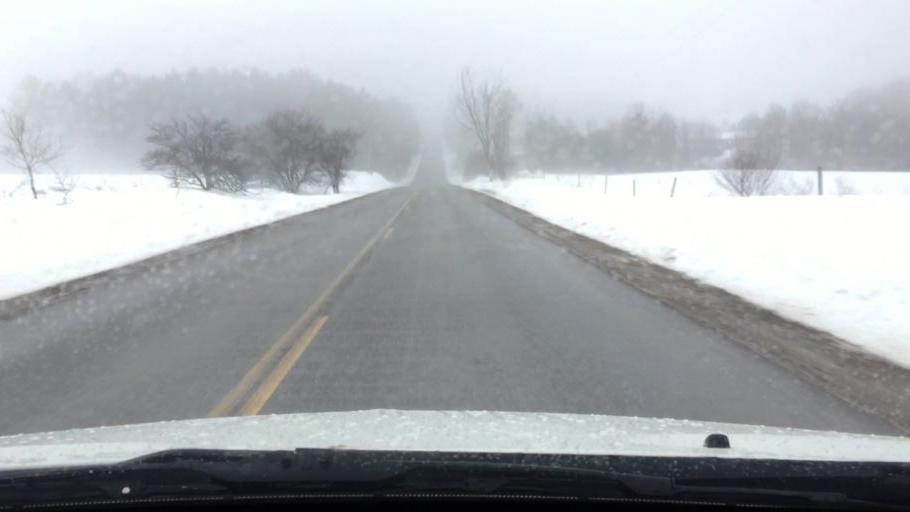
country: US
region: Michigan
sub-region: Charlevoix County
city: East Jordan
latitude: 45.1296
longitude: -85.1802
